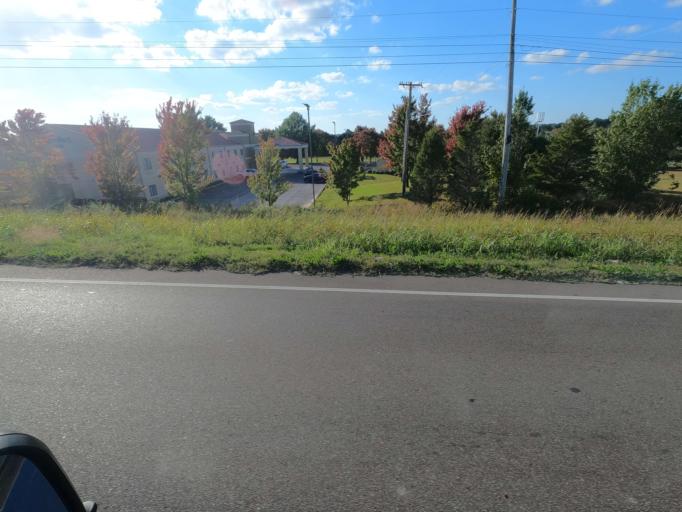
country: US
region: Tennessee
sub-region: Madison County
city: Jackson
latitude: 35.6823
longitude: -88.7794
